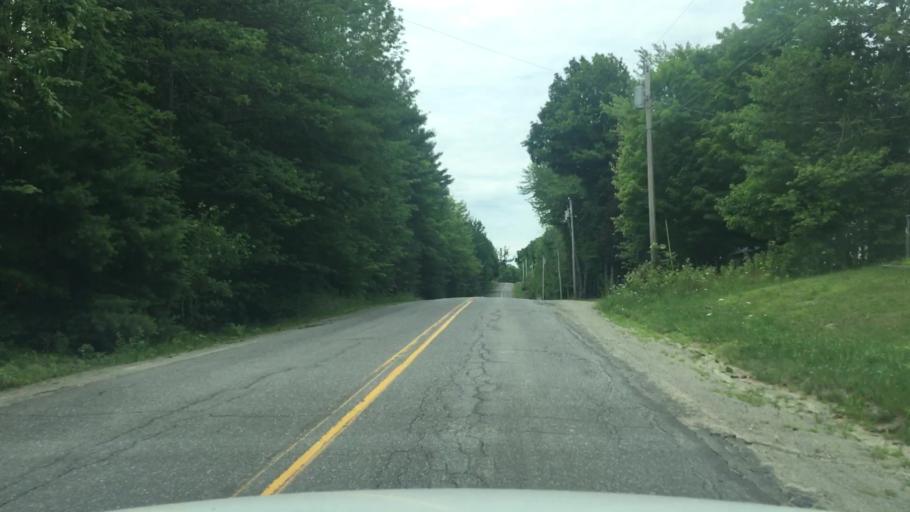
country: US
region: Maine
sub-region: Kennebec County
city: Albion
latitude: 44.5129
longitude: -69.3377
